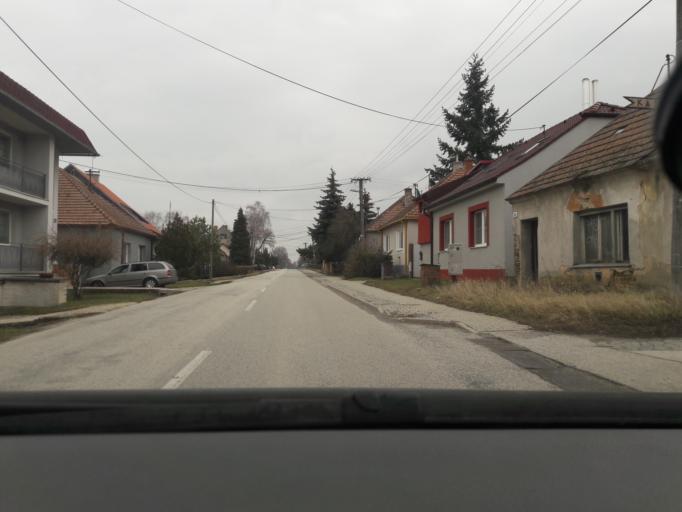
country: SK
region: Bratislavsky
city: Modra
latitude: 48.3644
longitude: 17.4010
